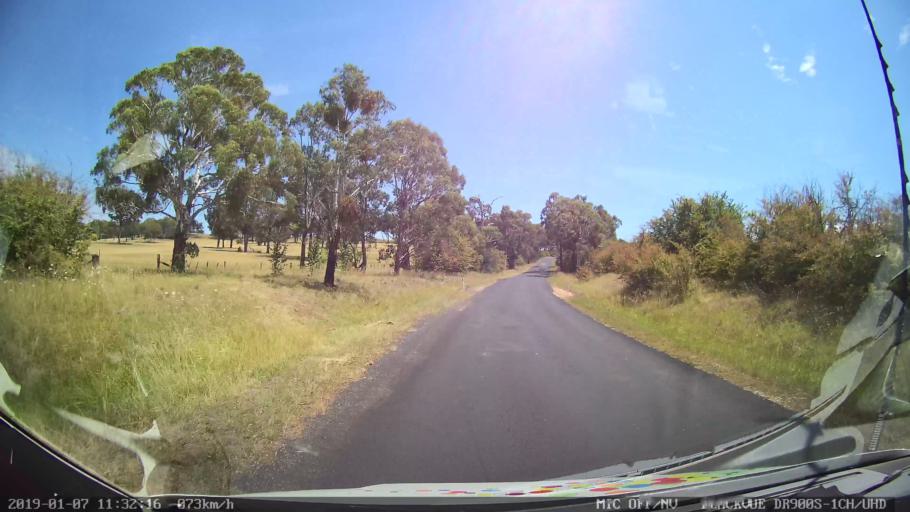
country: AU
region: New South Wales
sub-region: Armidale Dumaresq
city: Armidale
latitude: -30.4108
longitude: 151.5597
